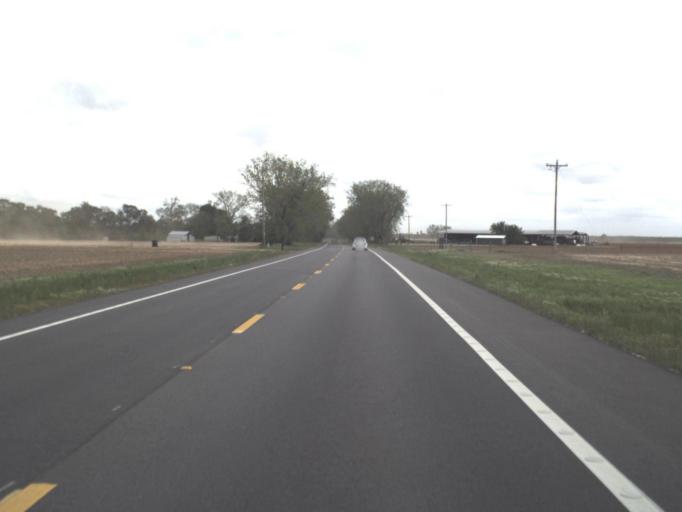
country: US
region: Florida
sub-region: Escambia County
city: Century
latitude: 30.8780
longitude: -87.1610
